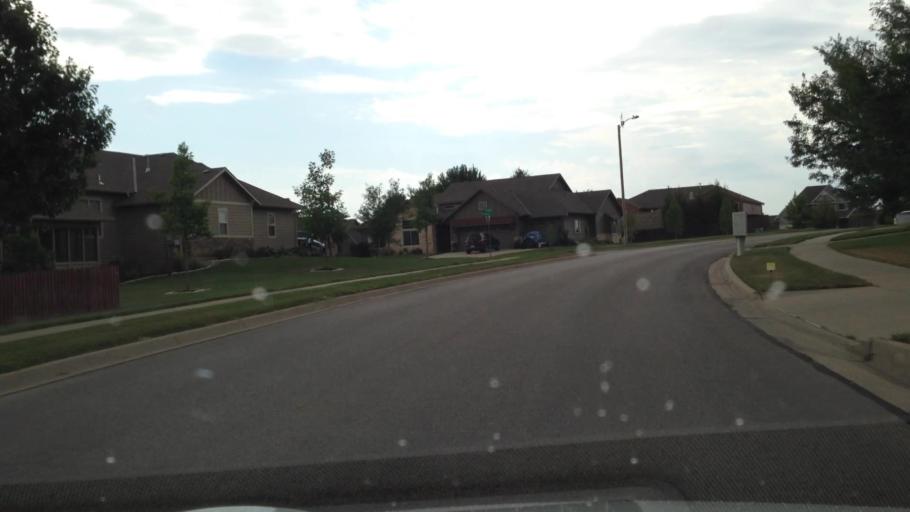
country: US
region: Kansas
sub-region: Douglas County
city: Lawrence
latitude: 38.9639
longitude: -95.3184
